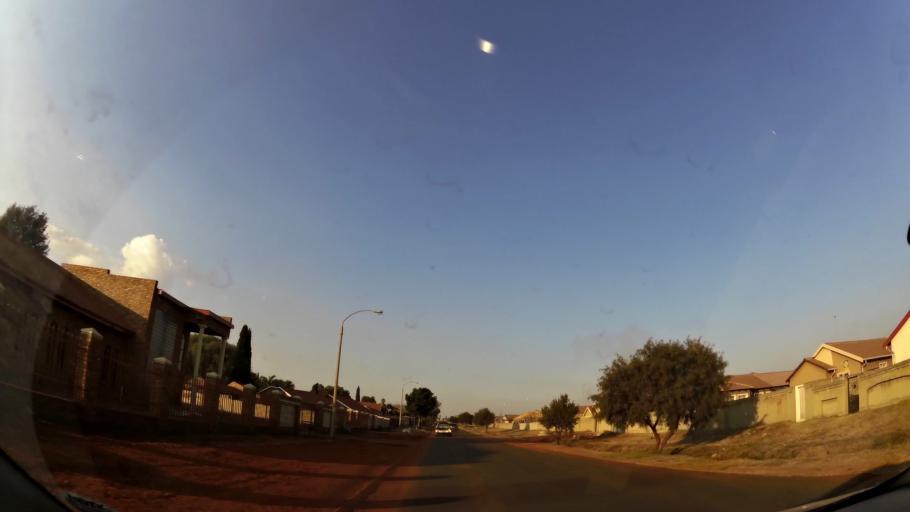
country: ZA
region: Gauteng
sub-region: Ekurhuleni Metropolitan Municipality
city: Boksburg
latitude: -26.3049
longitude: 28.2448
